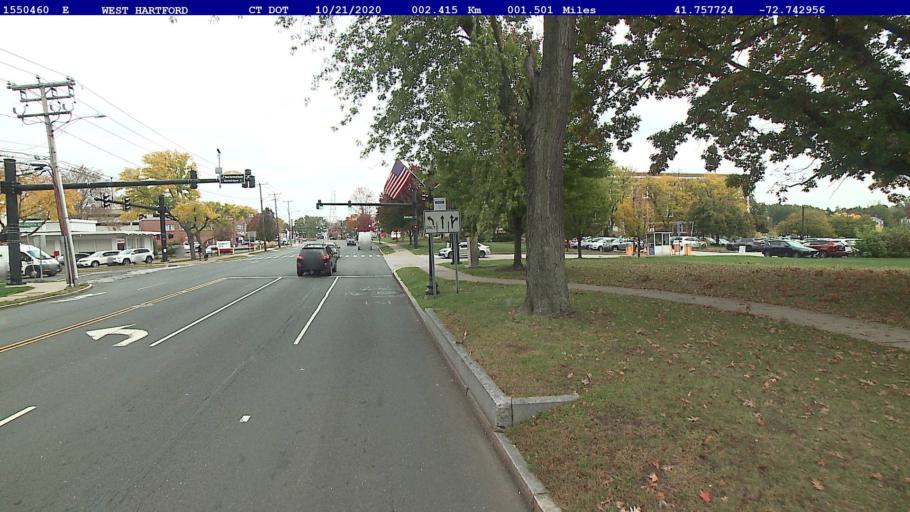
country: US
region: Connecticut
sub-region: Hartford County
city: West Hartford
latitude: 41.7577
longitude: -72.7430
